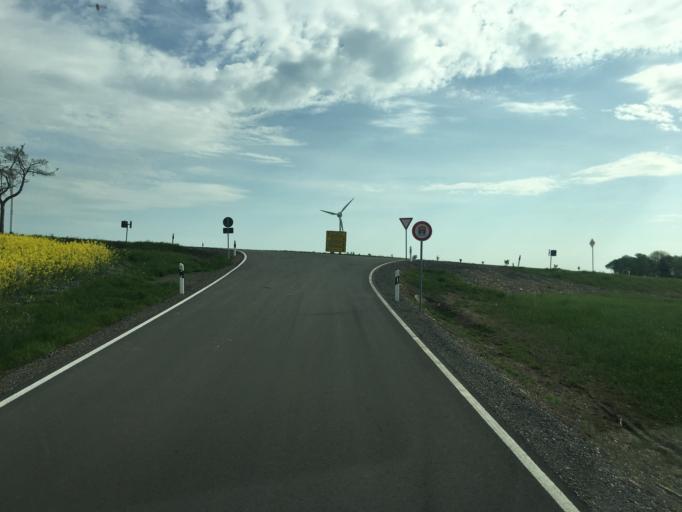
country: DE
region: Saxony
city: Schmiedeberg
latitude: 50.7371
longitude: 13.6465
